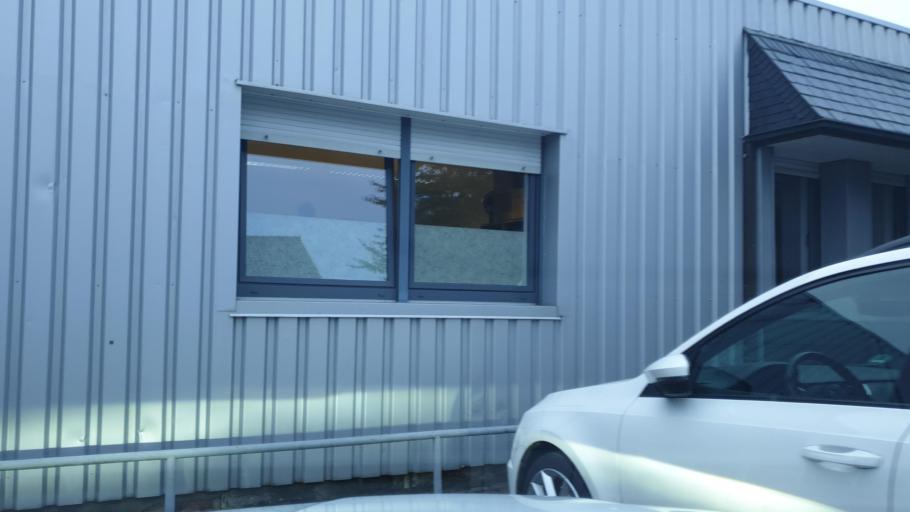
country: DE
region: North Rhine-Westphalia
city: Bad Oeynhausen
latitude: 52.1843
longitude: 8.8043
